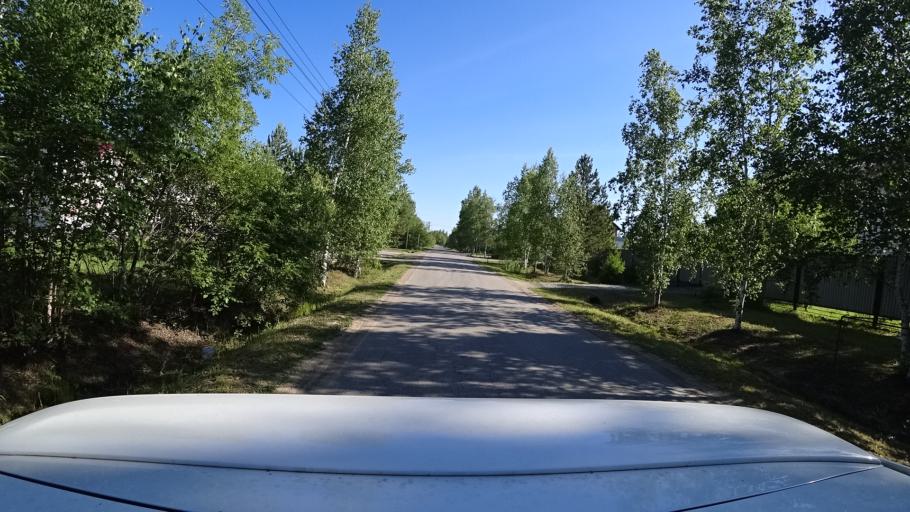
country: RU
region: Khabarovsk Krai
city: Topolevo
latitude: 48.5494
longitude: 135.1744
